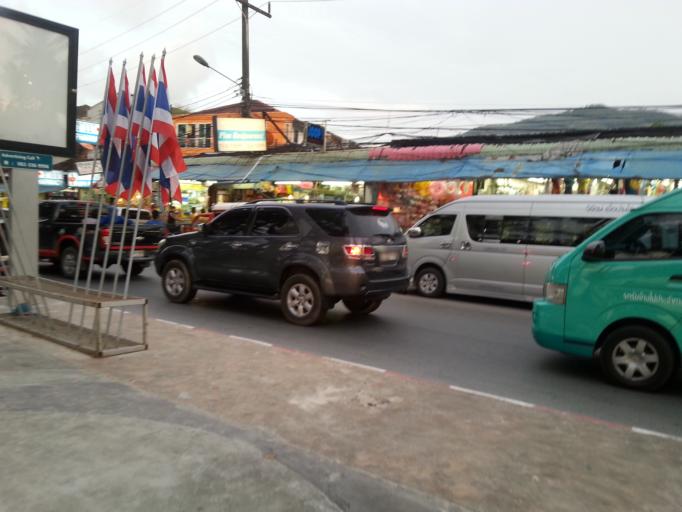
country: TH
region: Phuket
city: Patong
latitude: 7.8890
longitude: 98.2924
